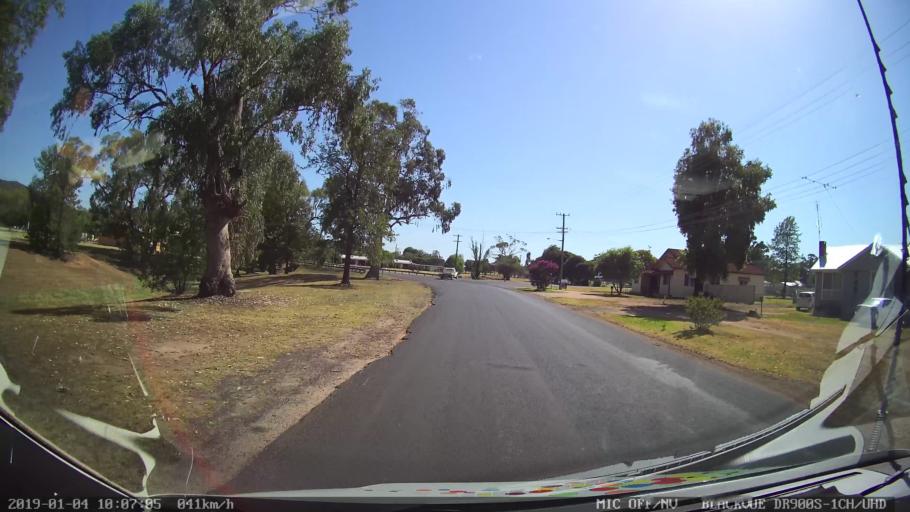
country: AU
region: New South Wales
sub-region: Cabonne
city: Canowindra
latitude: -33.4304
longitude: 148.3711
